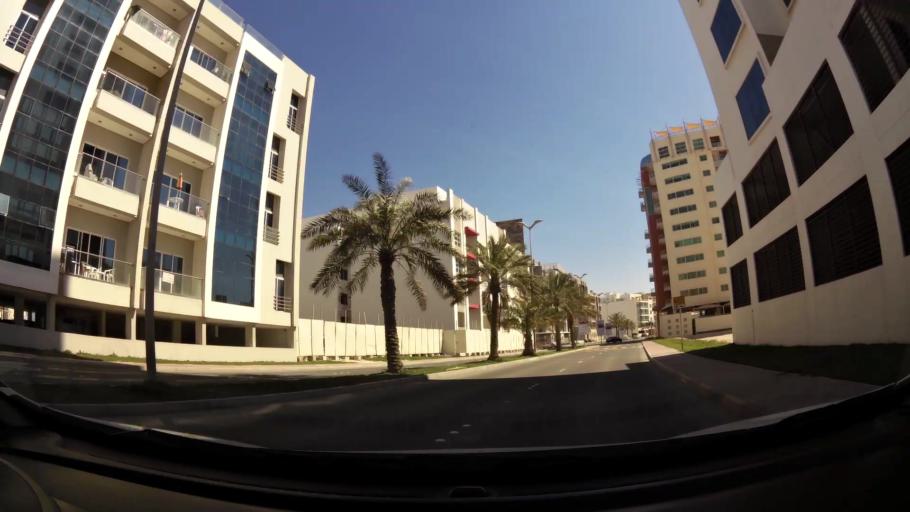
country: BH
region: Muharraq
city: Al Hadd
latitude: 26.2915
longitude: 50.6675
